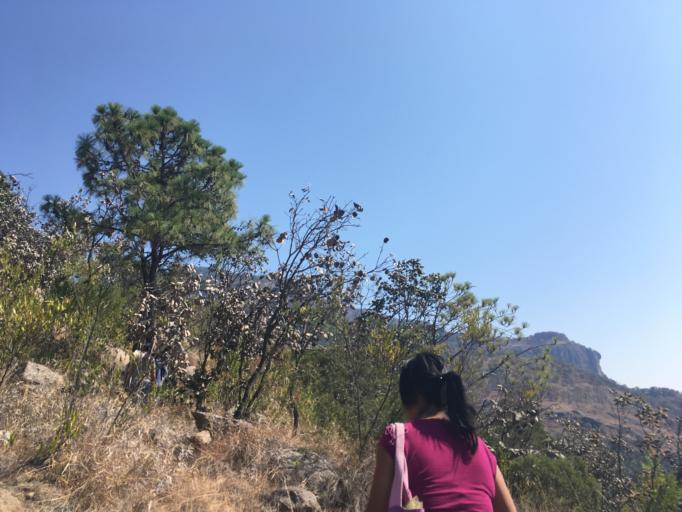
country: MX
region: Guerrero
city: Taxco de Alarcon
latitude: 18.5802
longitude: -99.6025
